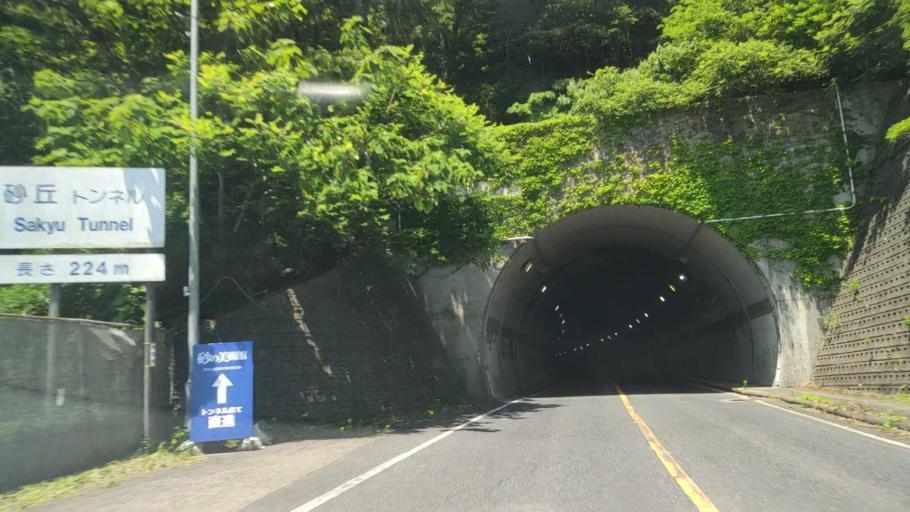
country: JP
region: Tottori
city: Tottori
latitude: 35.5305
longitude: 134.2291
